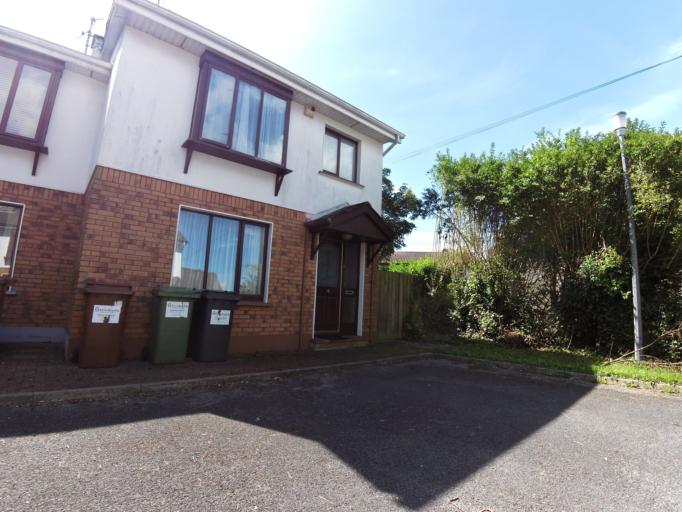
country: IE
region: Connaught
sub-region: County Galway
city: Gaillimh
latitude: 53.2728
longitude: -9.0754
